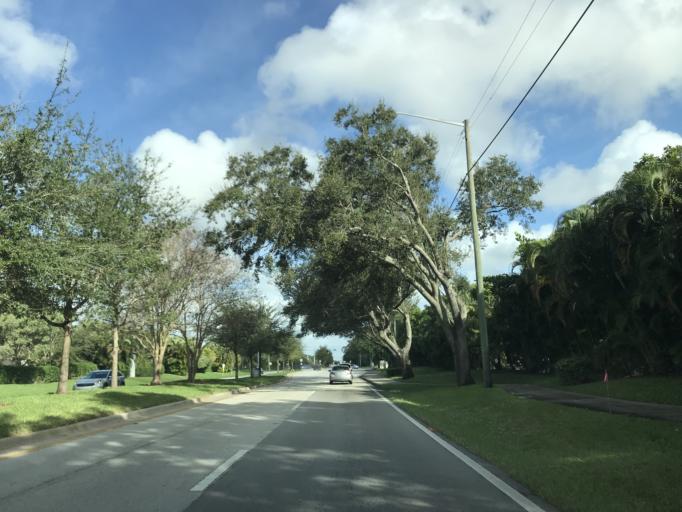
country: US
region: Florida
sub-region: Broward County
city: Coconut Creek
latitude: 26.2674
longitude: -80.1863
